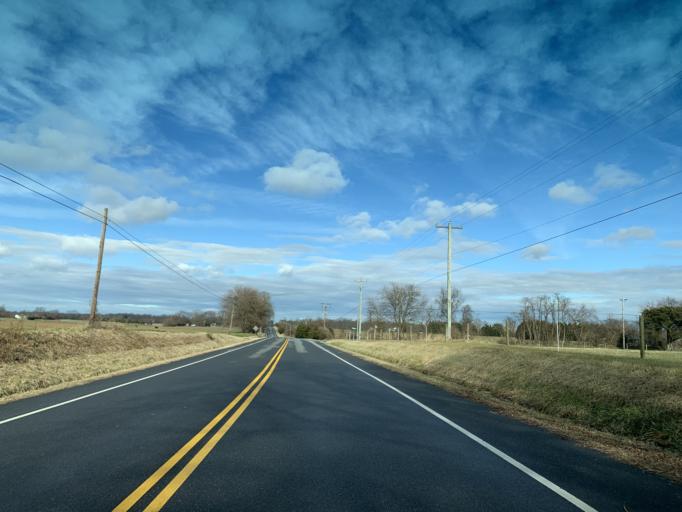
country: US
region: Maryland
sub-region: Harford County
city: Aberdeen Proving Ground
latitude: 39.3482
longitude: -76.0616
